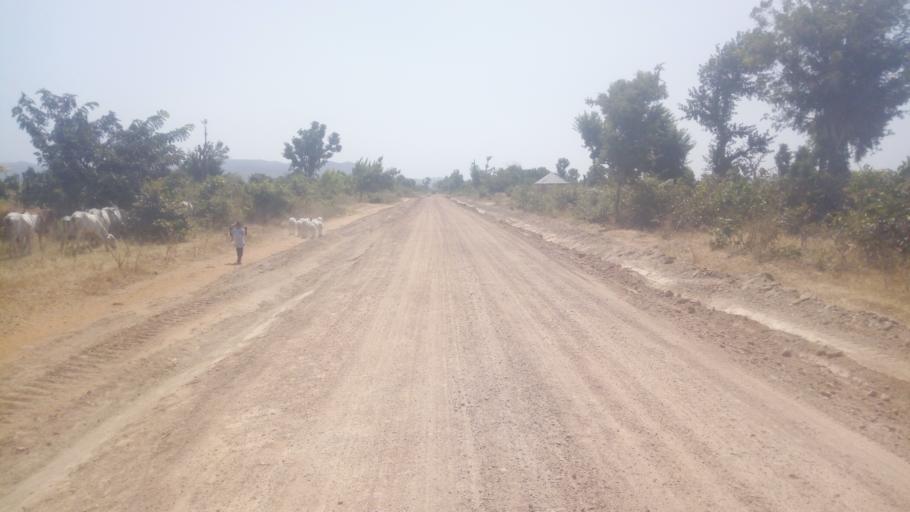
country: NG
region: Adamawa
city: Yola
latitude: 9.1722
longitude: 12.4028
